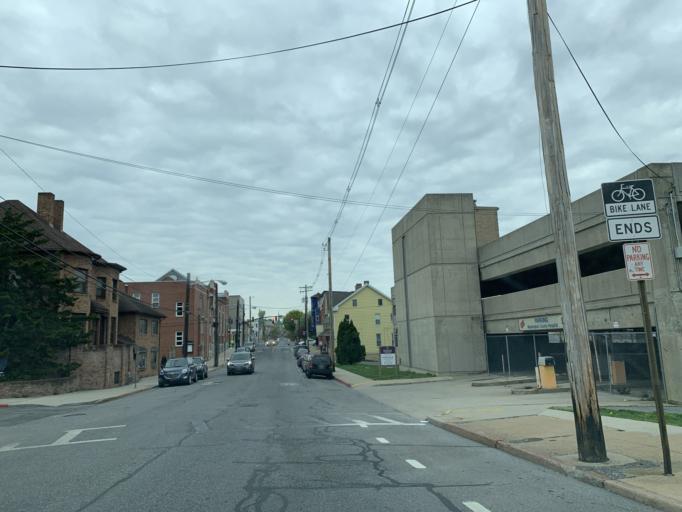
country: US
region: Maryland
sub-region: Washington County
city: Hagerstown
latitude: 39.6383
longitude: -77.7161
